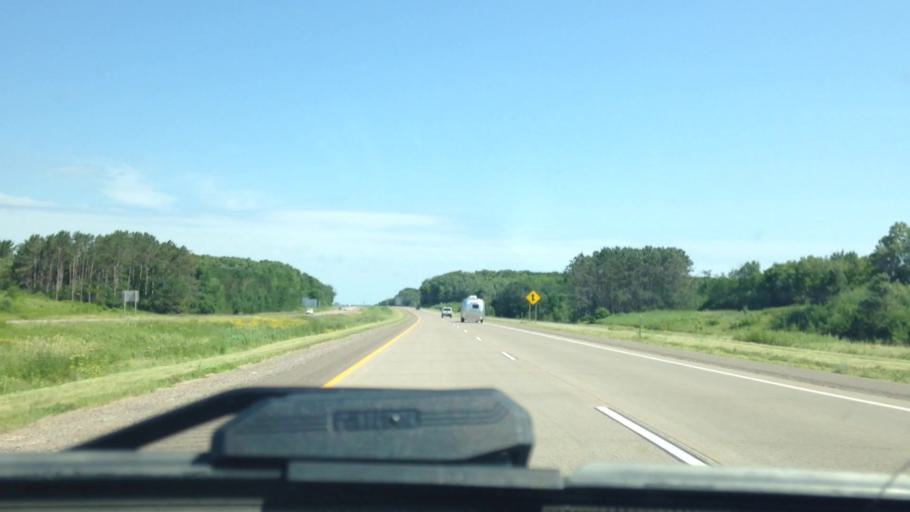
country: US
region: Wisconsin
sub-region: Barron County
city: Rice Lake
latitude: 45.5108
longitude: -91.7613
